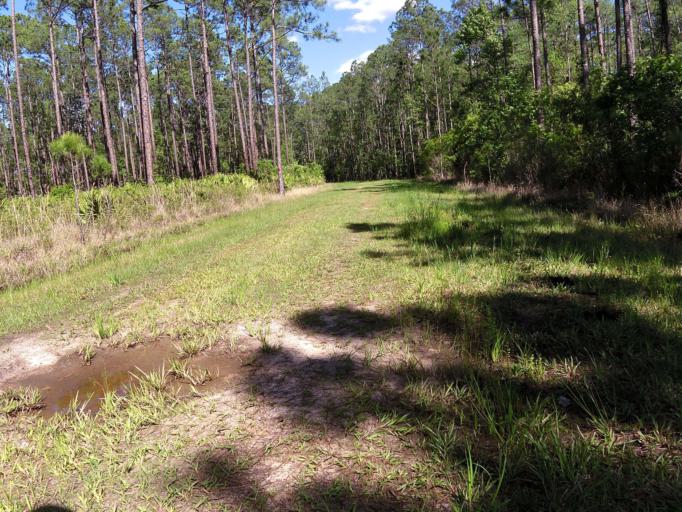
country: US
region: Florida
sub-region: Clay County
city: Green Cove Springs
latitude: 29.9563
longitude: -81.6212
